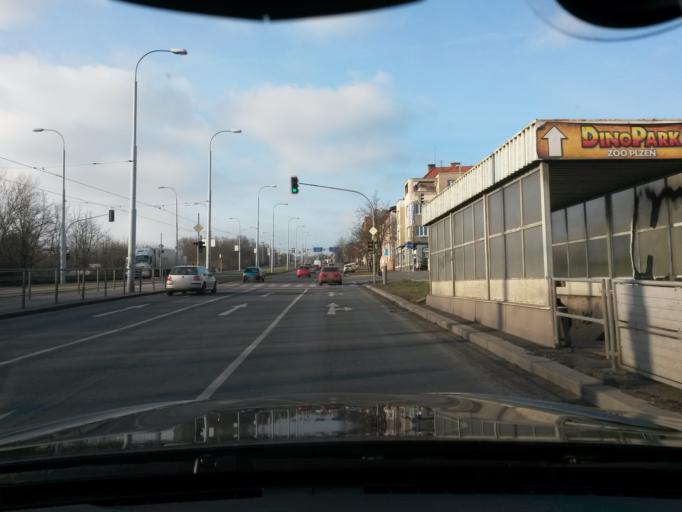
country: CZ
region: Plzensky
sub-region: Okres Plzen-Mesto
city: Pilsen
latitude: 49.7579
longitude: 13.3723
